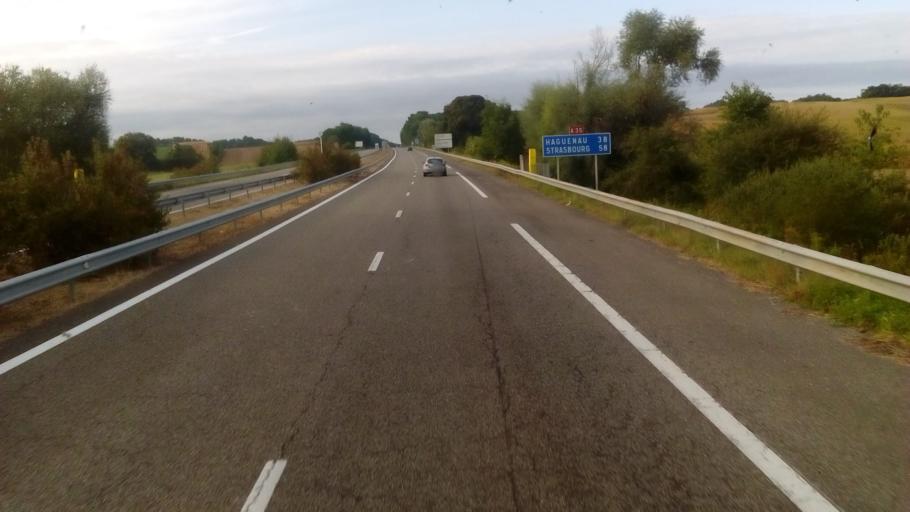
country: DE
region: Rheinland-Pfalz
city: Scheibenhardt
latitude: 48.9670
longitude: 8.1488
